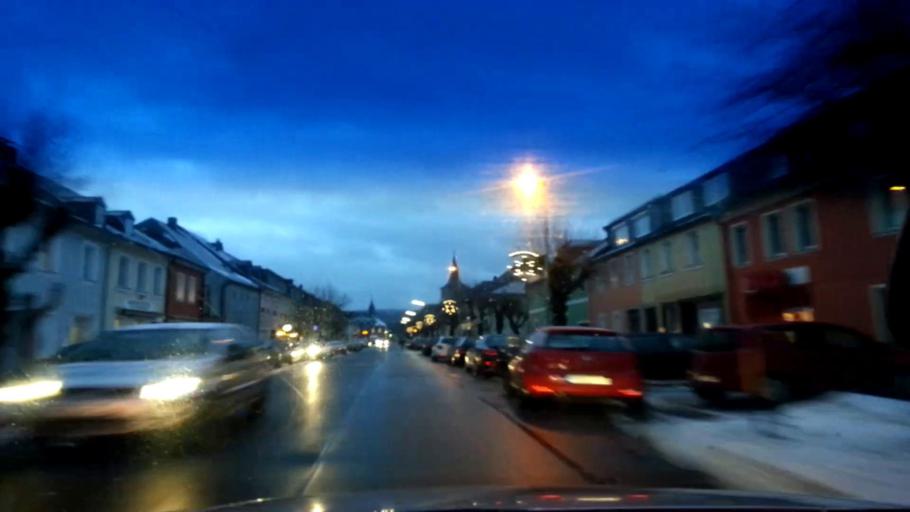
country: DE
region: Bavaria
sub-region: Upper Franconia
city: Weissenstadt
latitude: 50.1033
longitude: 11.8864
